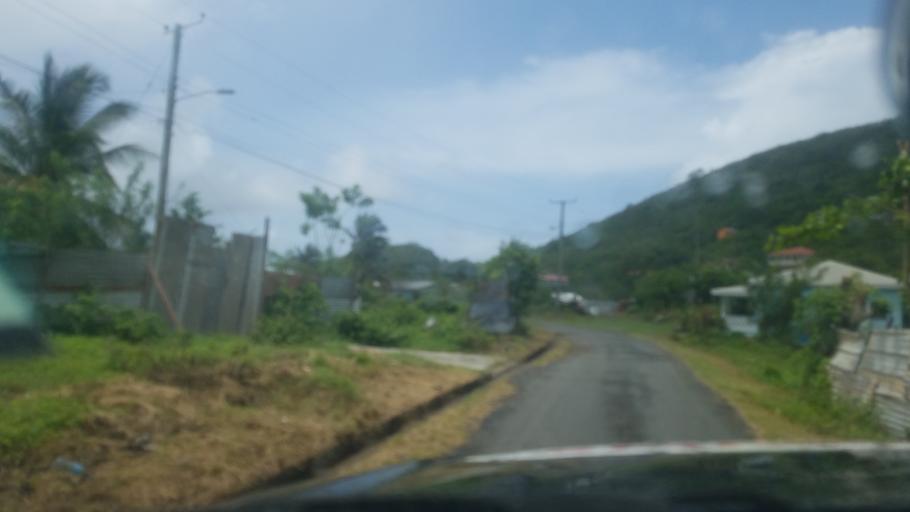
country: LC
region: Laborie Quarter
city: Laborie
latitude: 13.7476
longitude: -60.9647
